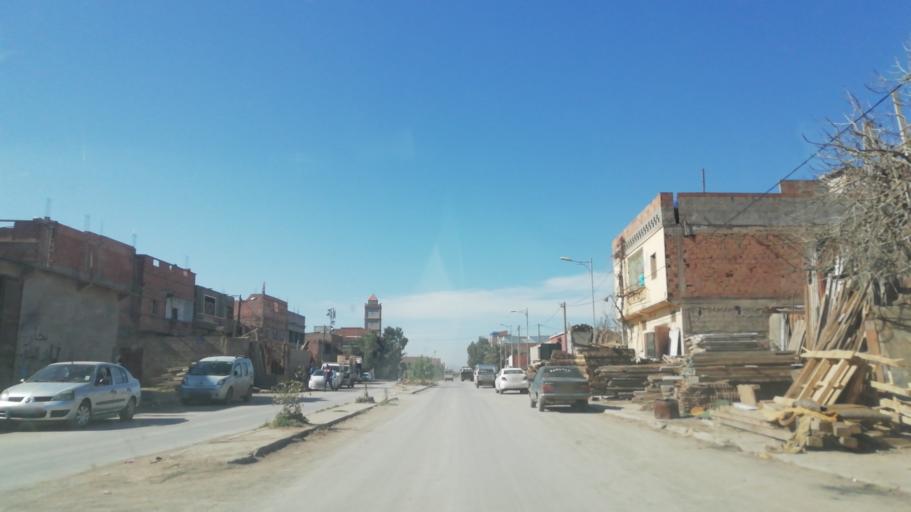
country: DZ
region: Oran
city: Es Senia
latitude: 35.6459
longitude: -0.5764
